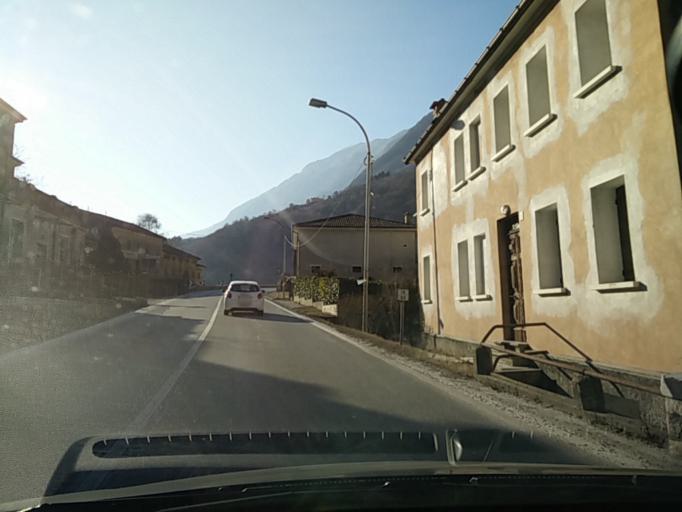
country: IT
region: Veneto
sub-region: Provincia di Belluno
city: Farra d'Alpago
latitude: 46.0785
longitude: 12.3362
